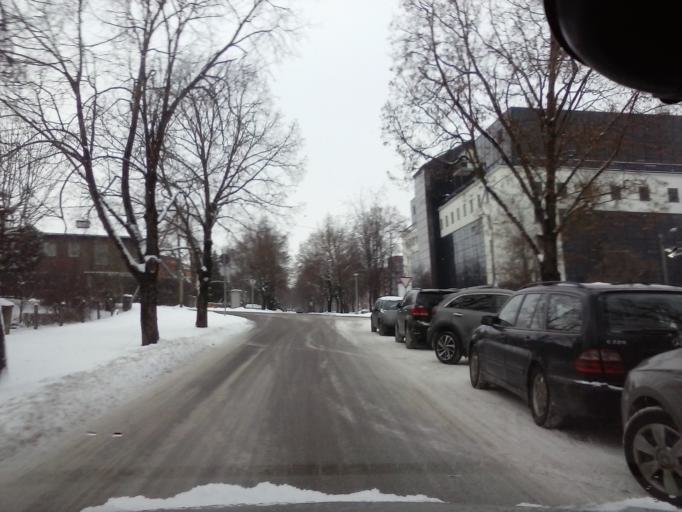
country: EE
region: Tartu
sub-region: Tartu linn
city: Tartu
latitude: 58.3662
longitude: 26.6965
